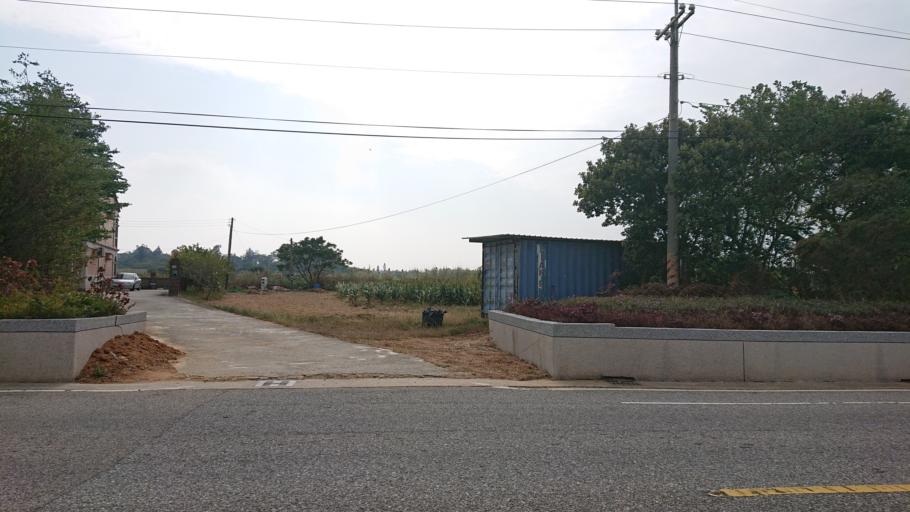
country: TW
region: Fukien
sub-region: Kinmen
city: Jincheng
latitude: 24.4528
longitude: 118.3803
